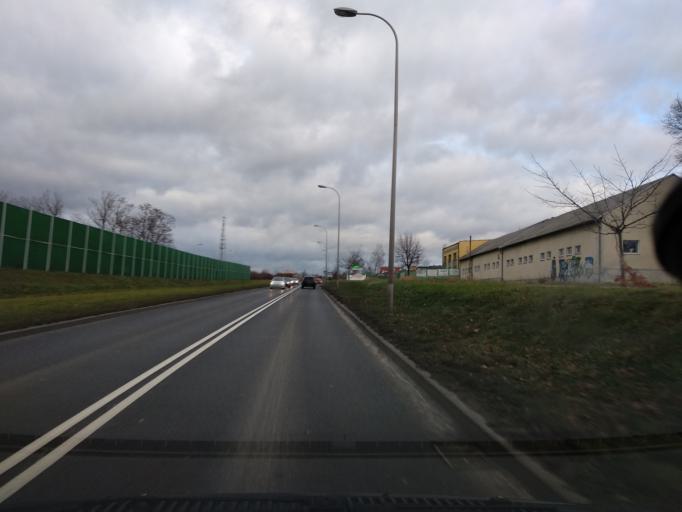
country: PL
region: Greater Poland Voivodeship
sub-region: Kalisz
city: Kalisz
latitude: 51.7762
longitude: 18.0775
